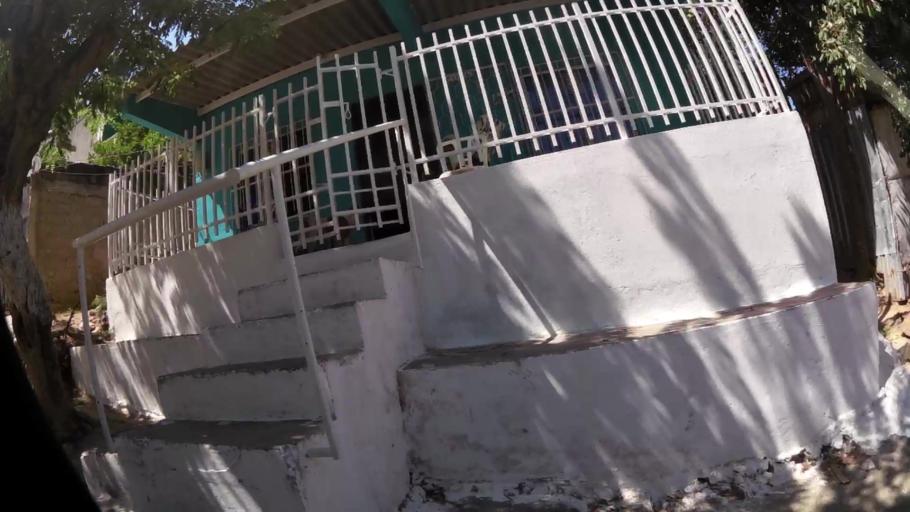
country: CO
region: Bolivar
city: Cartagena
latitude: 10.4284
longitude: -75.5300
